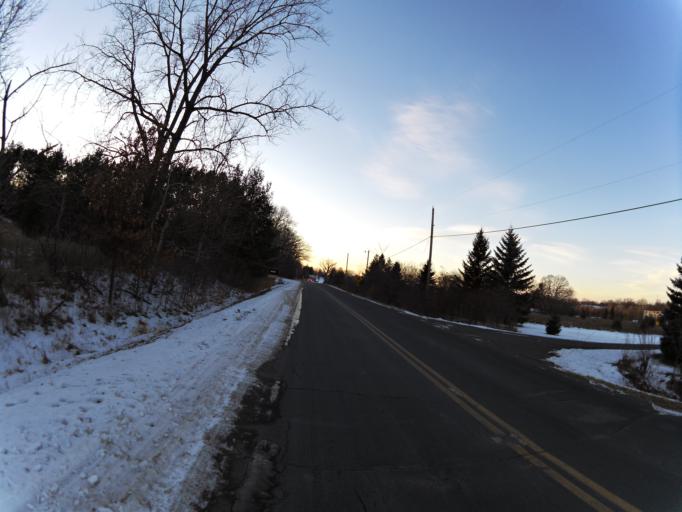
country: US
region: Minnesota
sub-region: Washington County
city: Lake Elmo
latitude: 44.9781
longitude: -92.8407
